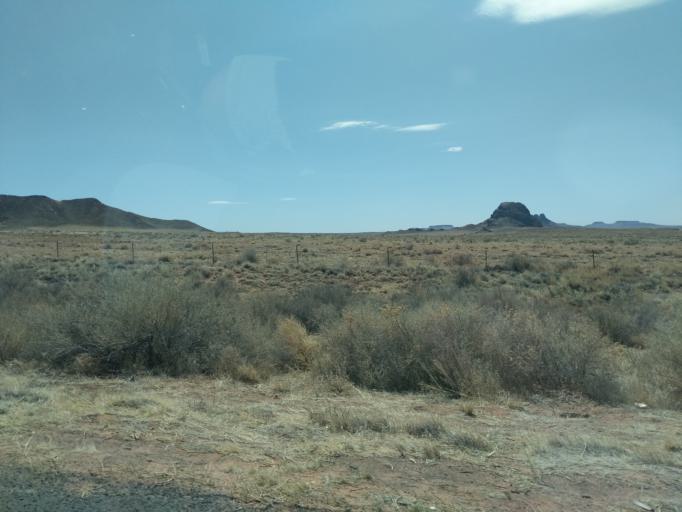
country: US
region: Arizona
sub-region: Navajo County
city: Dilkon
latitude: 35.4006
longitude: -110.0661
